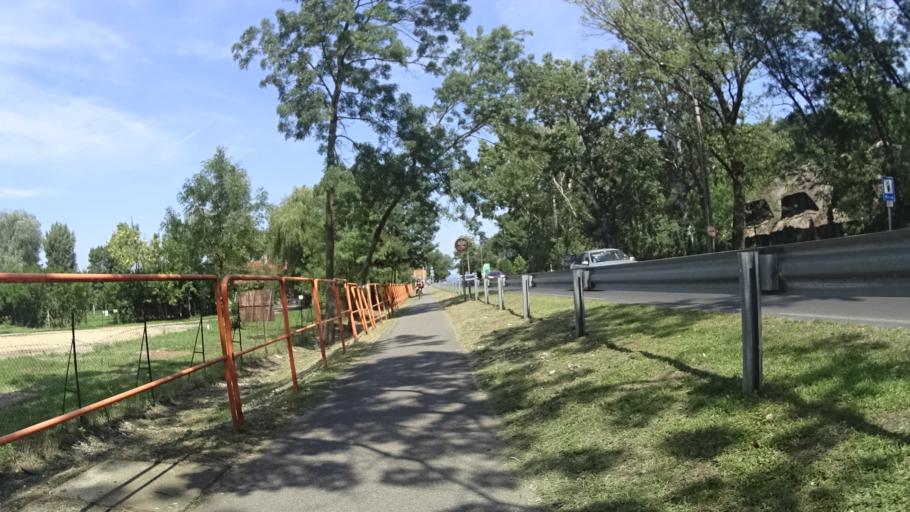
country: HU
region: Somogy
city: Balatonfenyves
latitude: 46.7355
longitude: 17.5347
